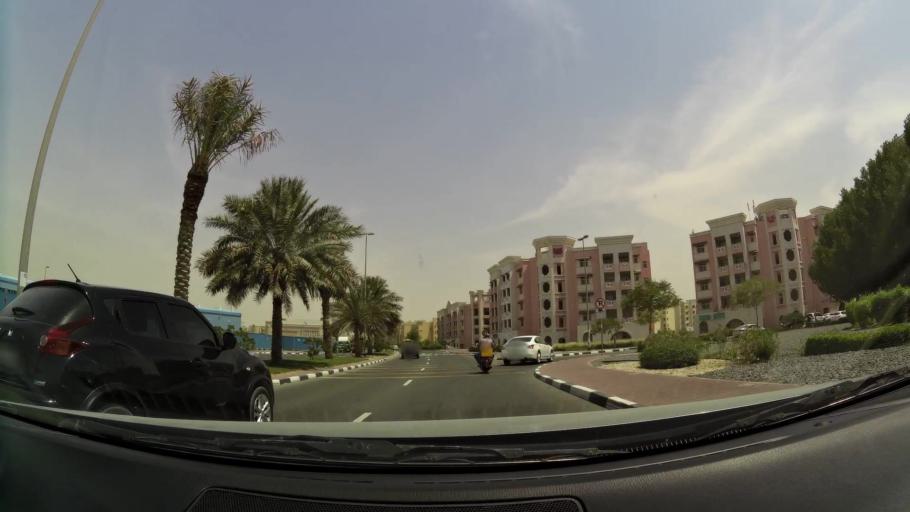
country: AE
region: Ash Shariqah
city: Sharjah
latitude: 25.1677
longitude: 55.4163
